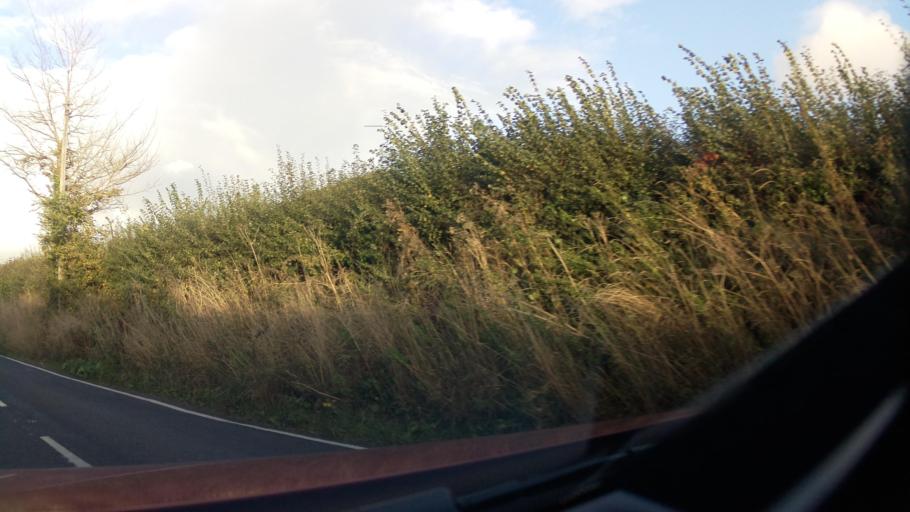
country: GB
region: England
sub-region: South Gloucestershire
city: Almondsbury
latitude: 51.5448
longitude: -2.5856
